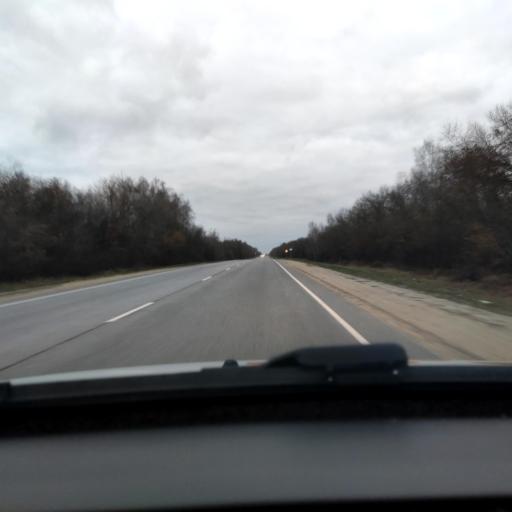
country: RU
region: Lipetsk
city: Khlevnoye
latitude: 52.3359
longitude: 39.1804
